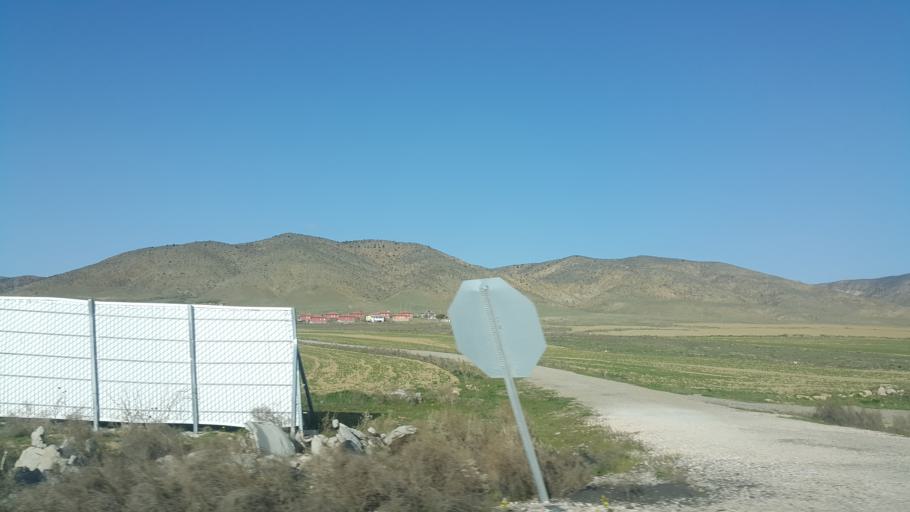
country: TR
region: Ankara
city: Sereflikochisar
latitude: 38.7514
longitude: 33.6603
